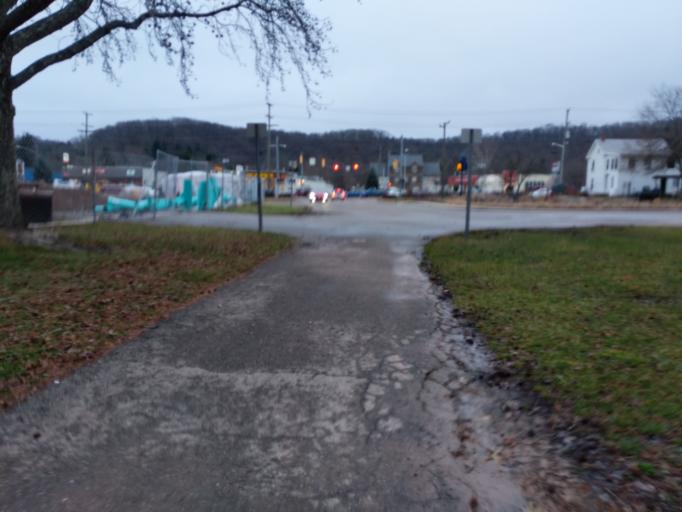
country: US
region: Ohio
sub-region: Athens County
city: Athens
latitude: 39.3367
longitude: -82.0767
